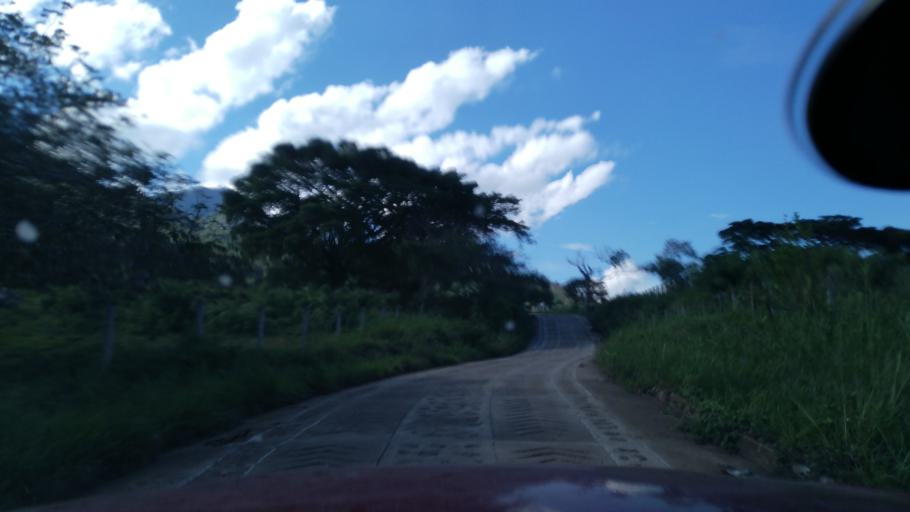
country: CO
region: Cundinamarca
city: Quipile
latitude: 4.7743
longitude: -74.6140
